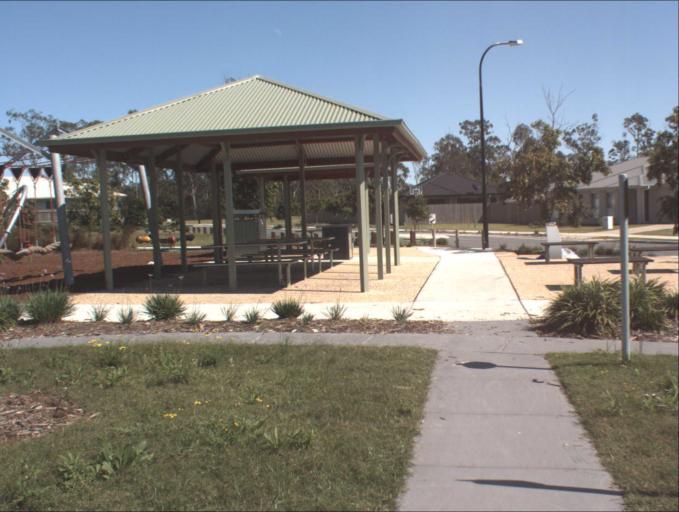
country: AU
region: Queensland
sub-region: Logan
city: North Maclean
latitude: -27.8034
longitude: 152.9603
